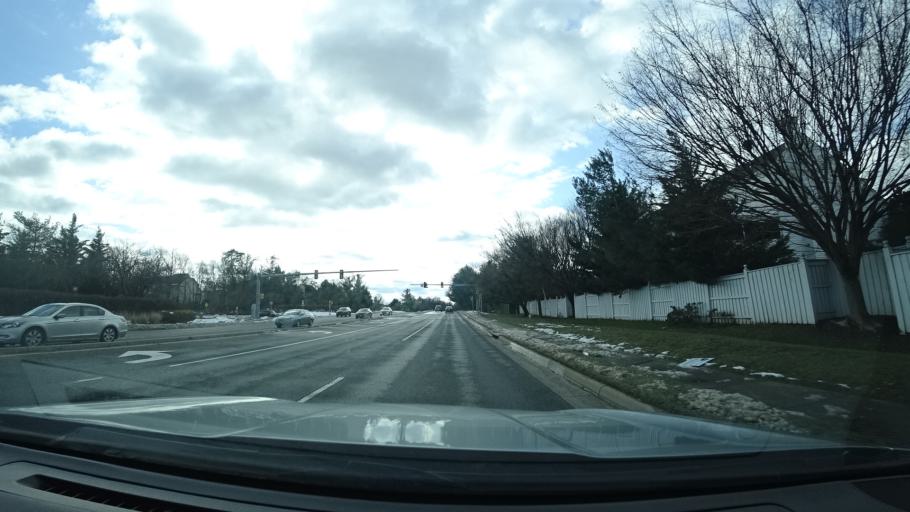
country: US
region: Virginia
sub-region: Loudoun County
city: Sugarland Run
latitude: 39.0368
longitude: -77.3573
